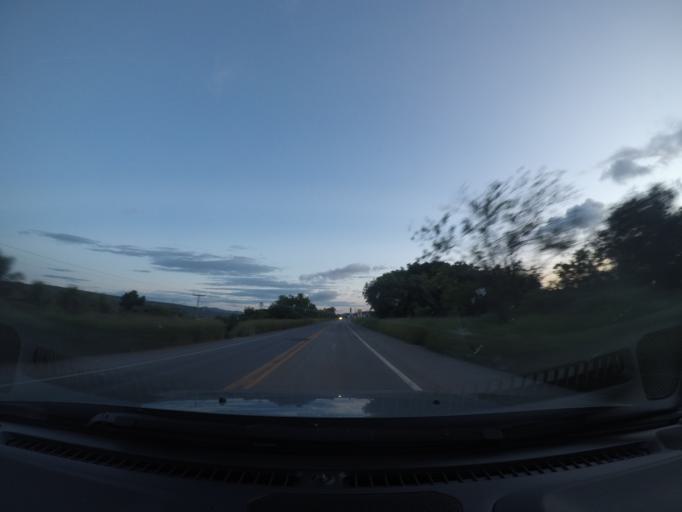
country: BR
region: Bahia
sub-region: Seabra
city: Seabra
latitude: -12.4464
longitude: -41.7517
